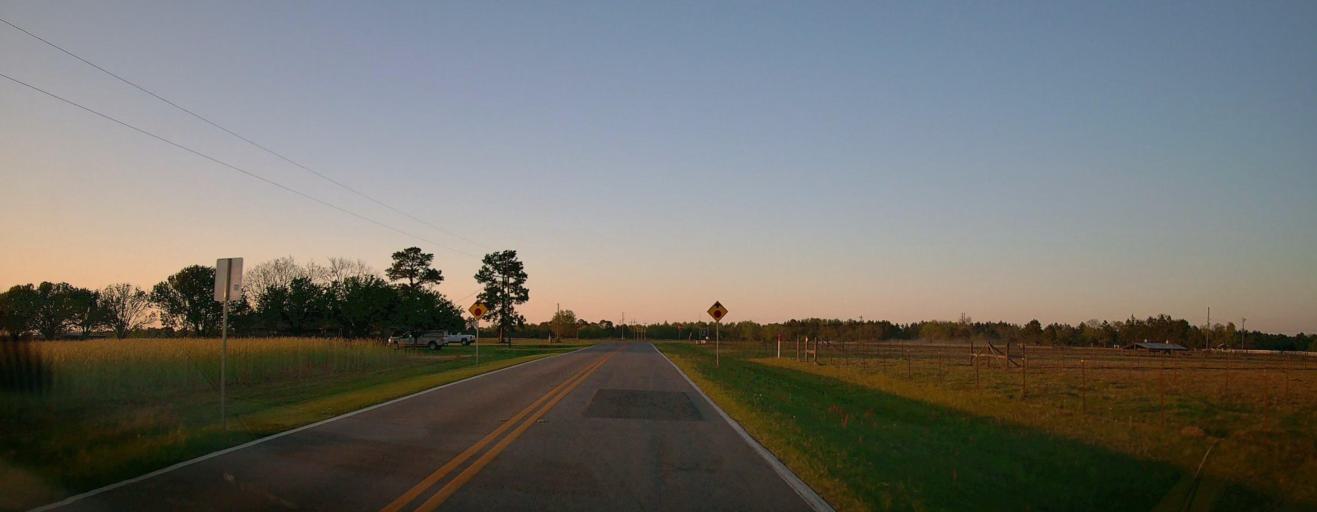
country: US
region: Georgia
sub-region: Ben Hill County
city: Fitzgerald
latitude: 31.7425
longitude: -83.3097
